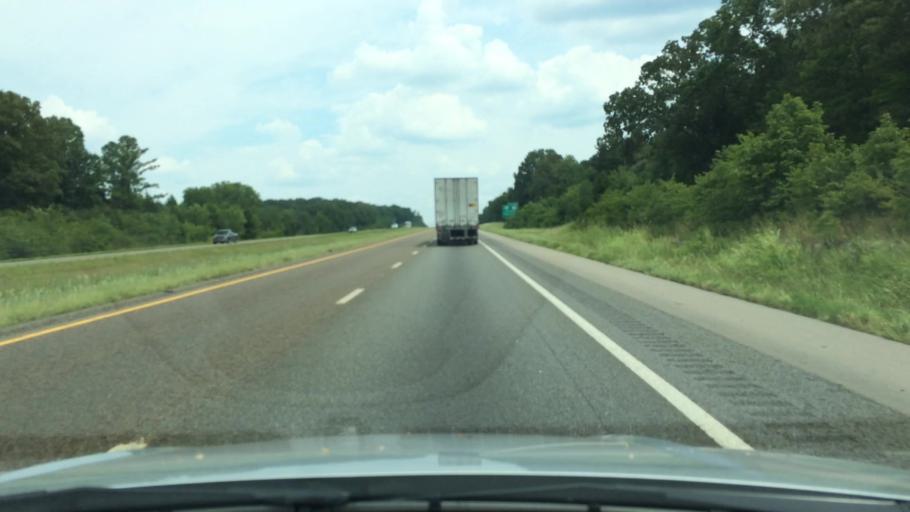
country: US
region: Tennessee
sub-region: Maury County
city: Spring Hill
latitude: 35.6250
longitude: -86.8979
